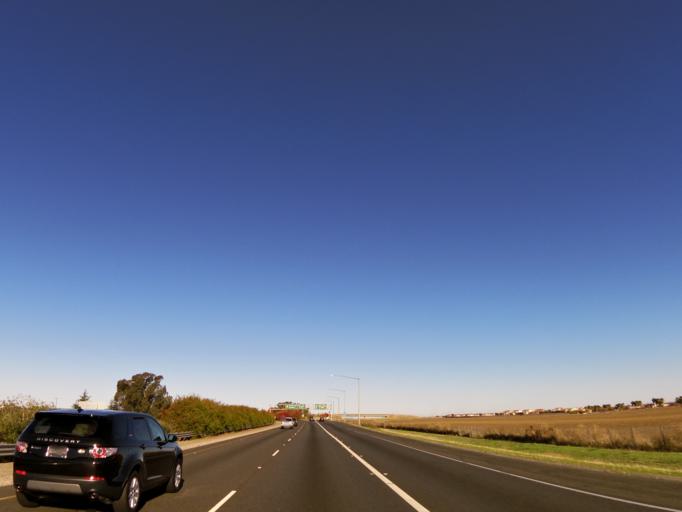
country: US
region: California
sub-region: Yolo County
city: West Sacramento
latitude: 38.6635
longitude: -121.5370
